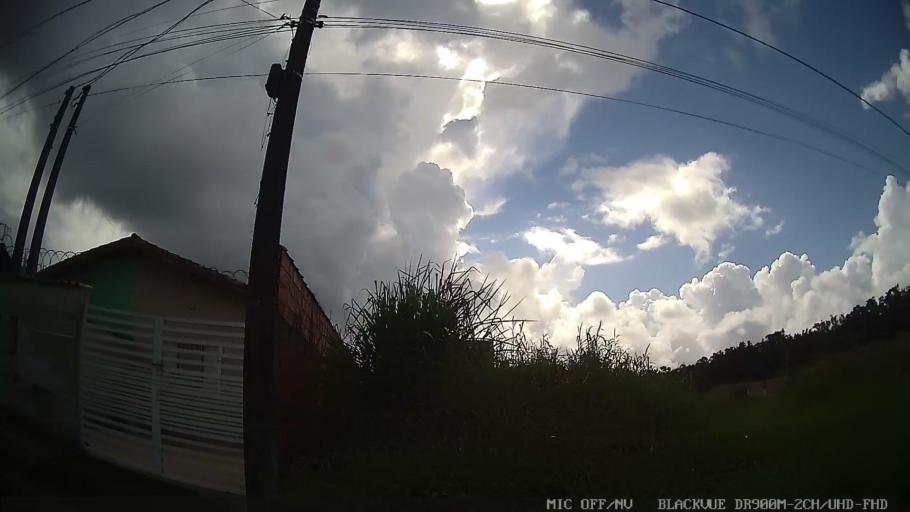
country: BR
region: Sao Paulo
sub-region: Itanhaem
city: Itanhaem
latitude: -24.2065
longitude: -46.8488
